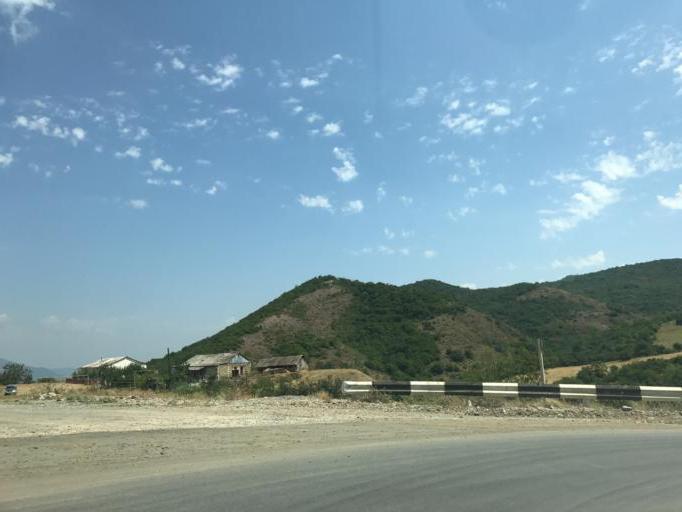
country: AZ
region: Tartar Rayon
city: Martakert
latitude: 40.1299
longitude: 46.6236
